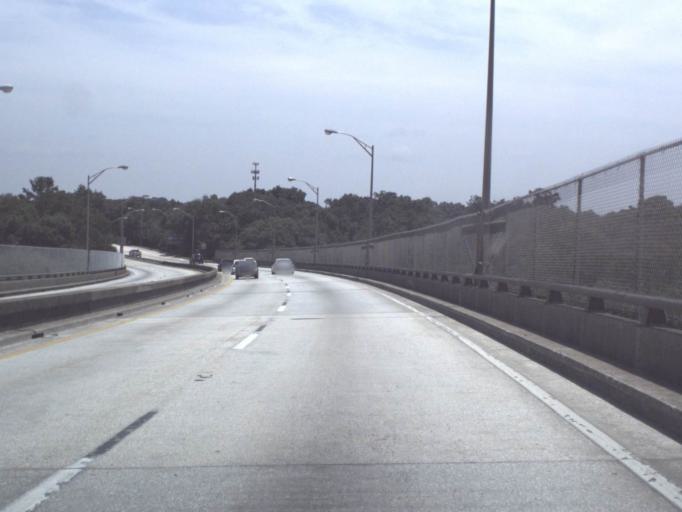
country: US
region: Florida
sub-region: Duval County
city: Jacksonville
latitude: 30.3111
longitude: -81.6243
